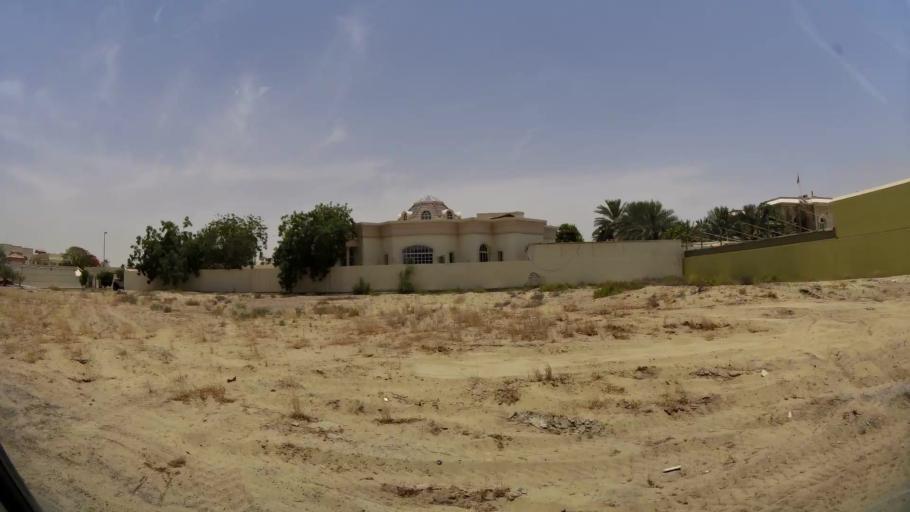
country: AE
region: Ash Shariqah
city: Sharjah
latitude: 25.2334
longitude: 55.4562
